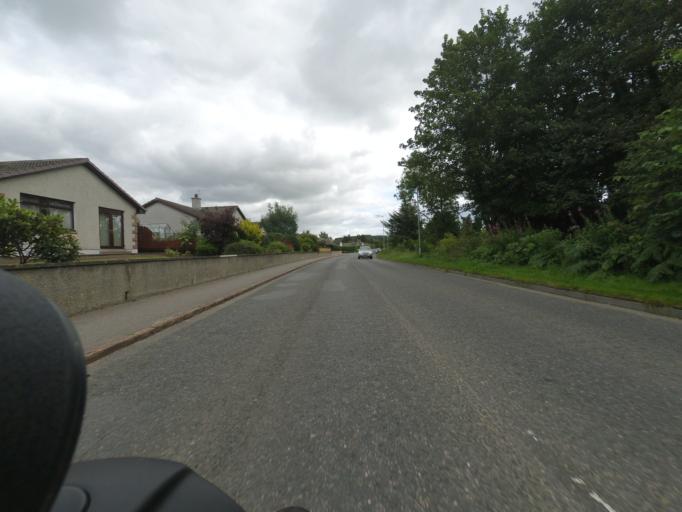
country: GB
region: Scotland
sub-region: Aberdeenshire
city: Banchory
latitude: 57.0569
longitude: -2.4734
